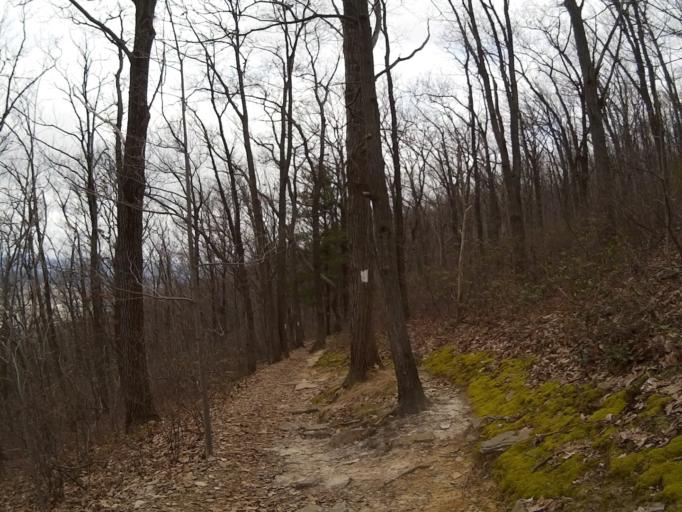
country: US
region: Pennsylvania
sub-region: Centre County
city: Lemont
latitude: 40.8097
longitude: -77.8011
